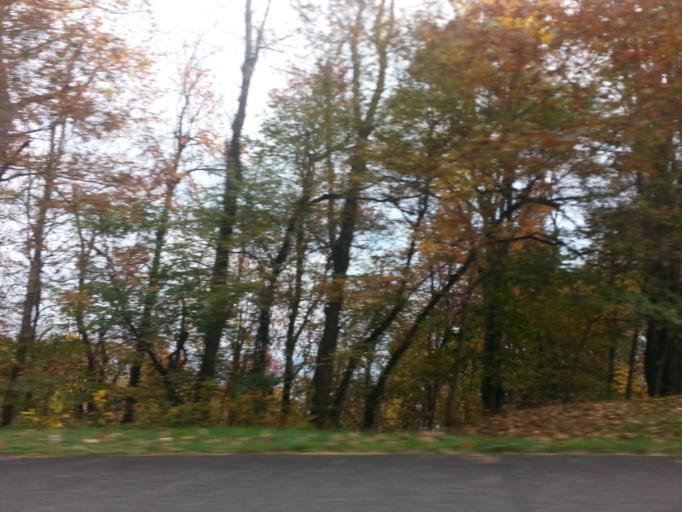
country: US
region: North Carolina
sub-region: Ashe County
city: Jefferson
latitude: 36.2988
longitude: -81.3664
